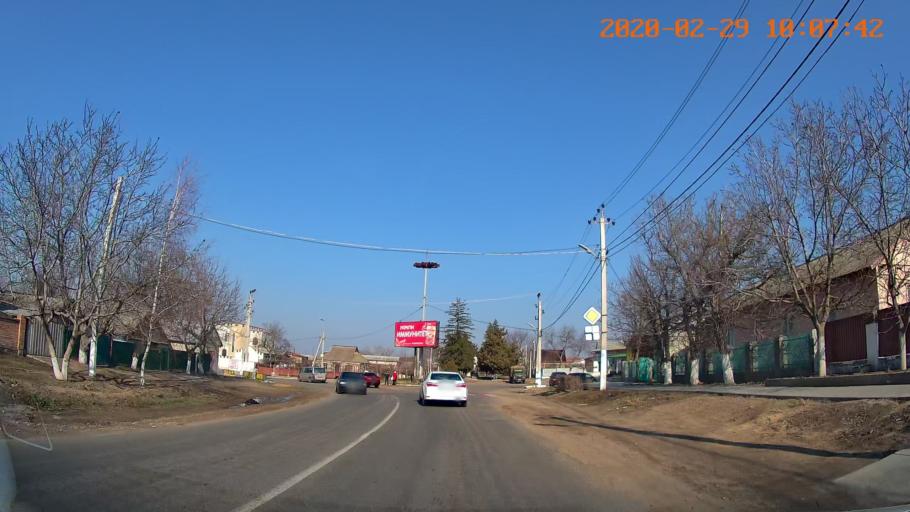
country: MD
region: Telenesti
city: Tiraspolul Nou
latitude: 46.8226
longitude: 29.6638
